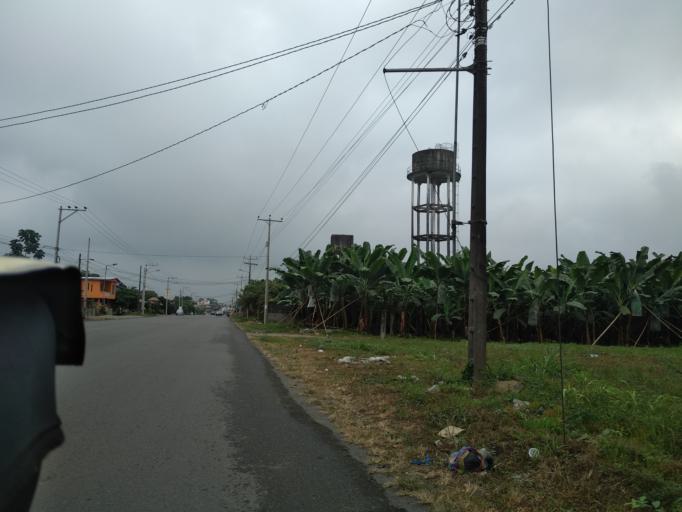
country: EC
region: Cotopaxi
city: La Mana
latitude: -0.9449
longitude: -79.3297
